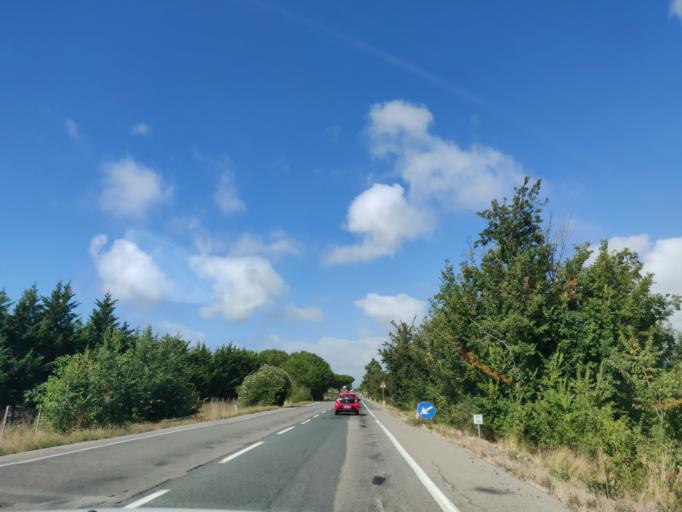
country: IT
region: Tuscany
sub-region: Provincia di Grosseto
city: Capalbio
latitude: 42.4152
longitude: 11.3577
